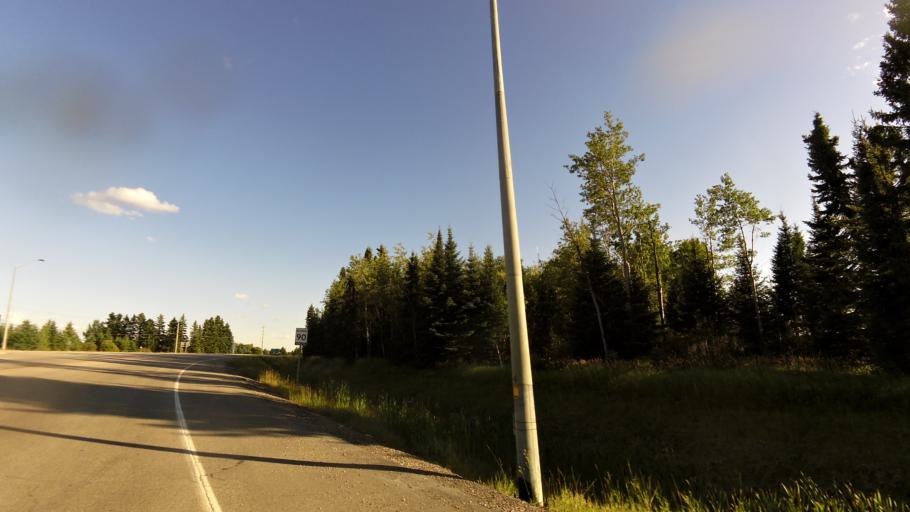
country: CA
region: Ontario
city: Dryden
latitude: 49.8136
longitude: -92.8485
